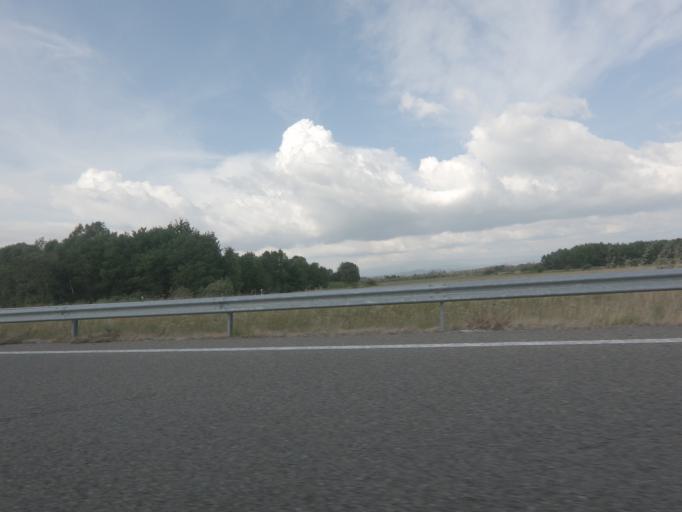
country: ES
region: Galicia
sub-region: Provincia de Ourense
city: Ambia
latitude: 42.1399
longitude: -7.7453
